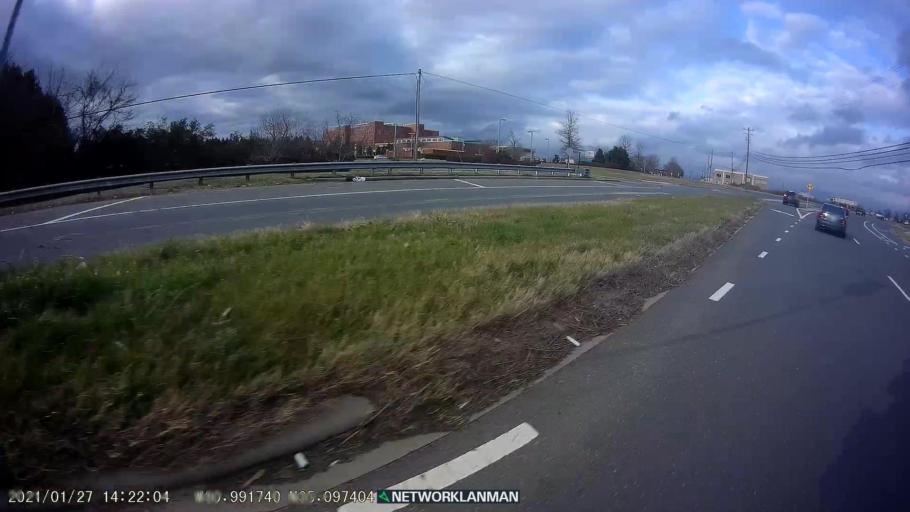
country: US
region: South Carolina
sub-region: York County
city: Lake Wylie
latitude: 35.0977
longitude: -80.9913
